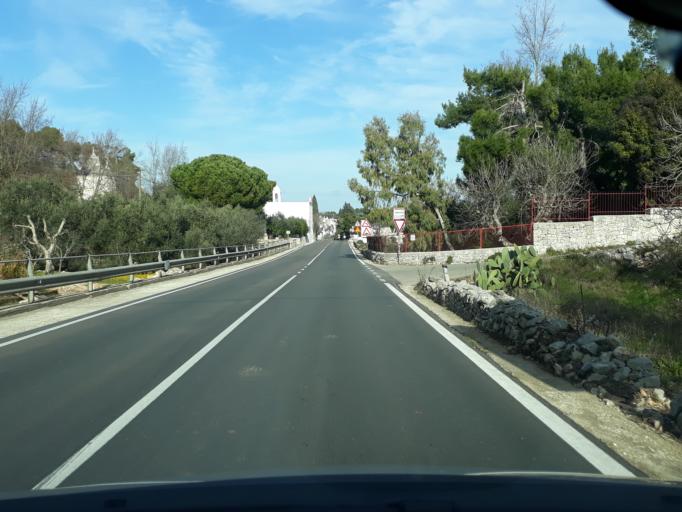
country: IT
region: Apulia
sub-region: Provincia di Brindisi
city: Lamie di Olimpie-Selva
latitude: 40.7922
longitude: 17.3470
